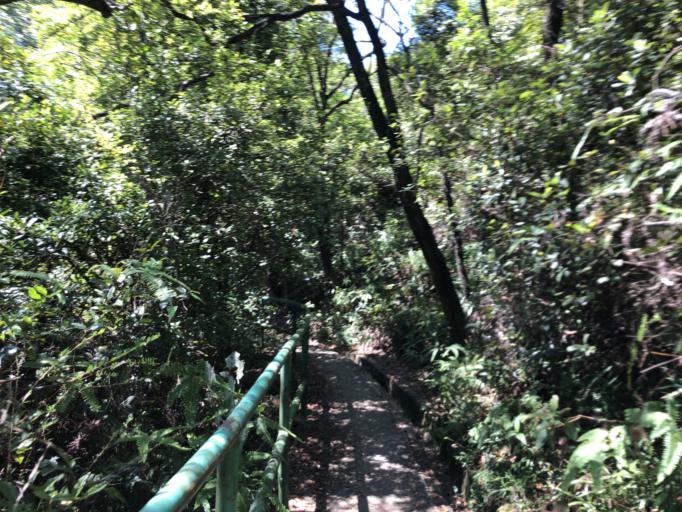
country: HK
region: Tuen Mun
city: Tuen Mun
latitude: 22.2796
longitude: 113.9871
